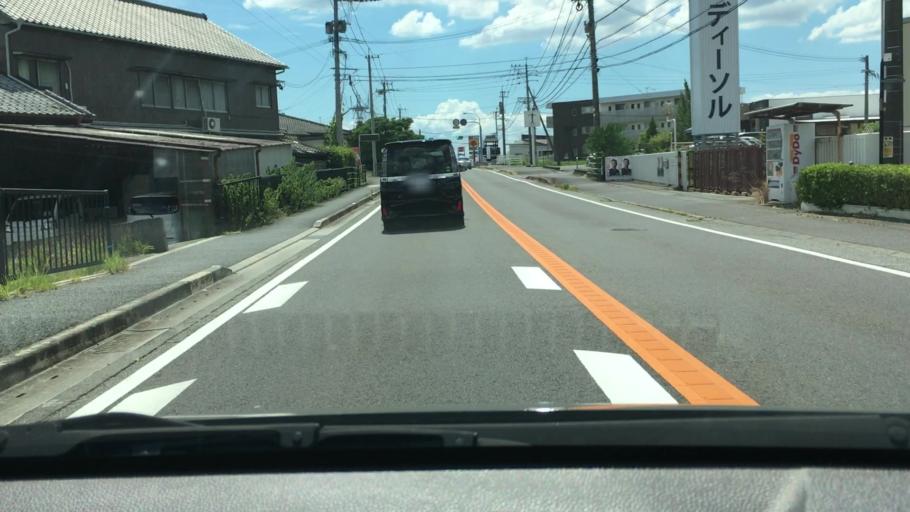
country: JP
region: Saga Prefecture
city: Kanzakimachi-kanzaki
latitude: 33.3169
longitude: 130.3801
